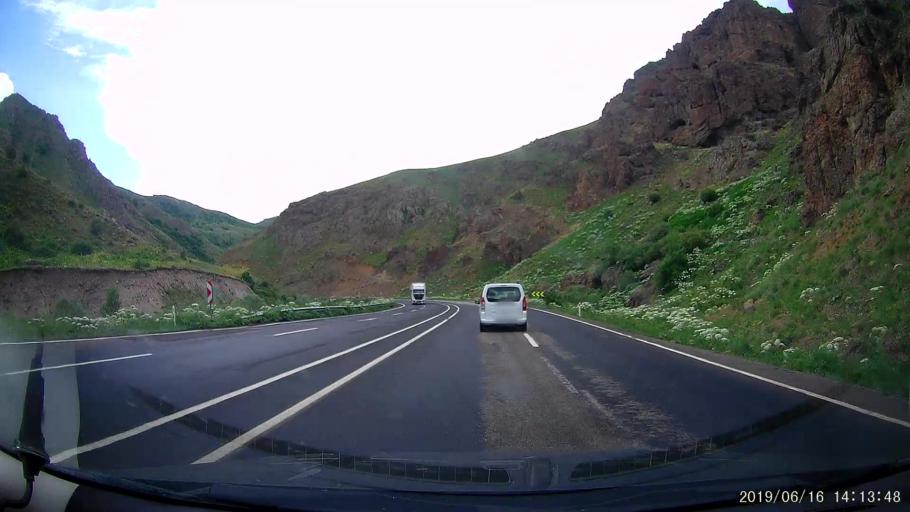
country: TR
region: Agri
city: Tahir
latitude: 39.7961
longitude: 42.5090
